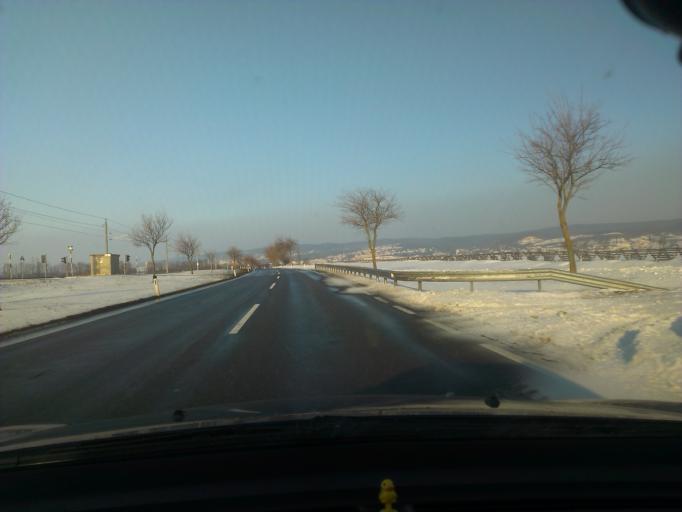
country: AT
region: Burgenland
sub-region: Eisenstadt-Umgebung
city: Trausdorf an der Wulka
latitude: 47.8430
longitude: 16.5686
